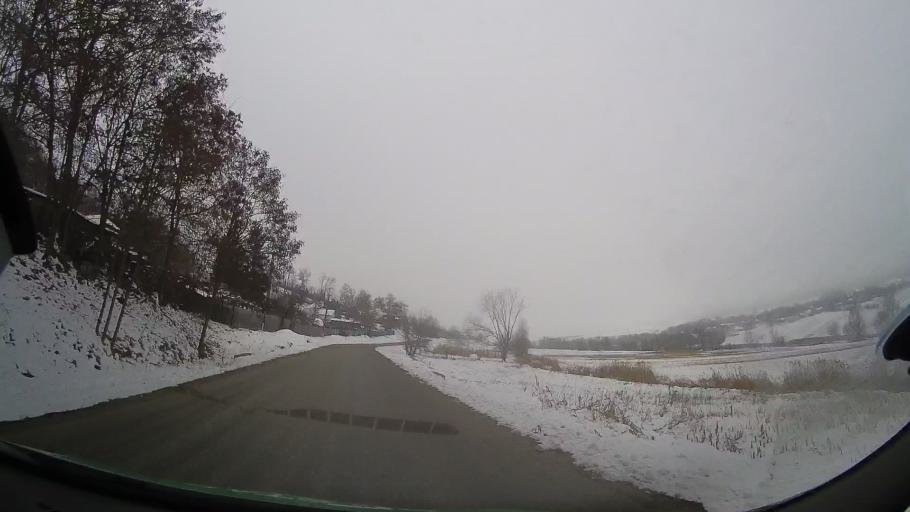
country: RO
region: Bacau
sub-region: Comuna Vultureni
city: Vultureni
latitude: 46.3337
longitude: 27.2916
